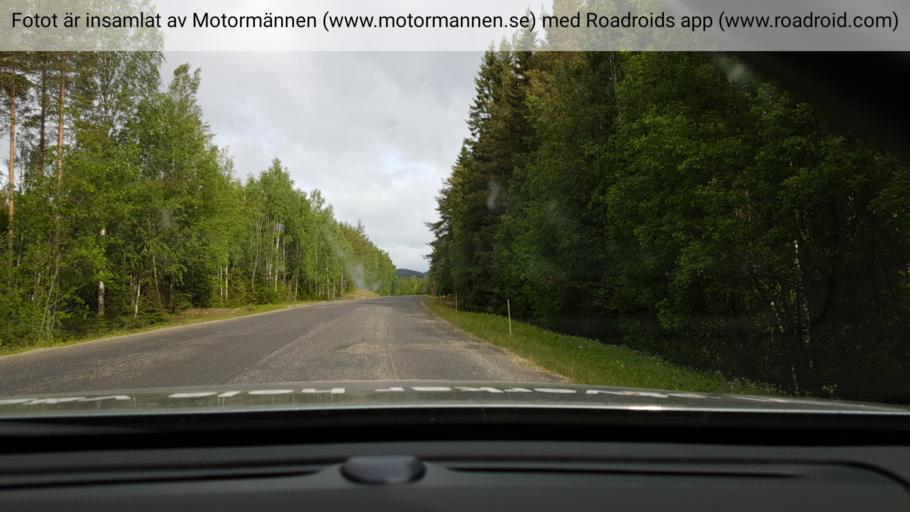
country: SE
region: Vaesterbotten
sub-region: Bjurholms Kommun
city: Bjurholm
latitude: 63.9212
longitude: 19.1147
